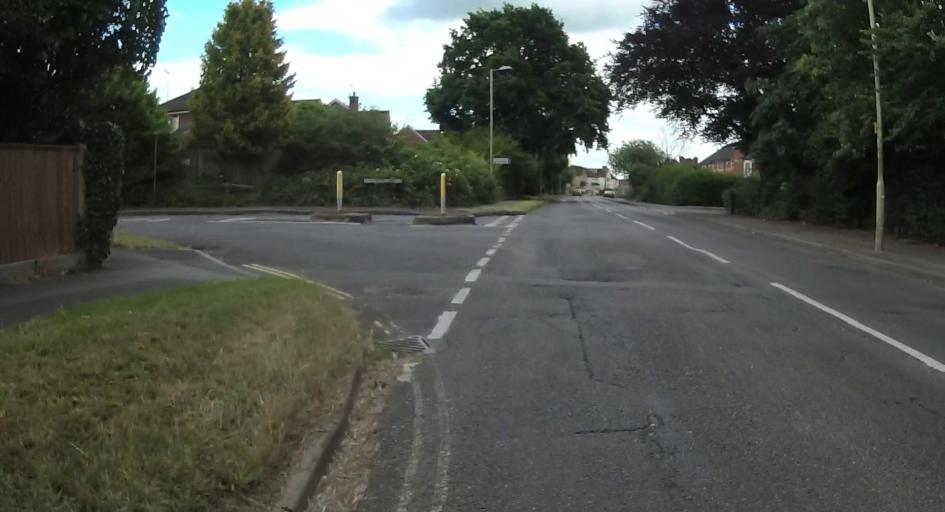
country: GB
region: England
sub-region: Hampshire
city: Aldershot
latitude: 51.2372
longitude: -0.7640
